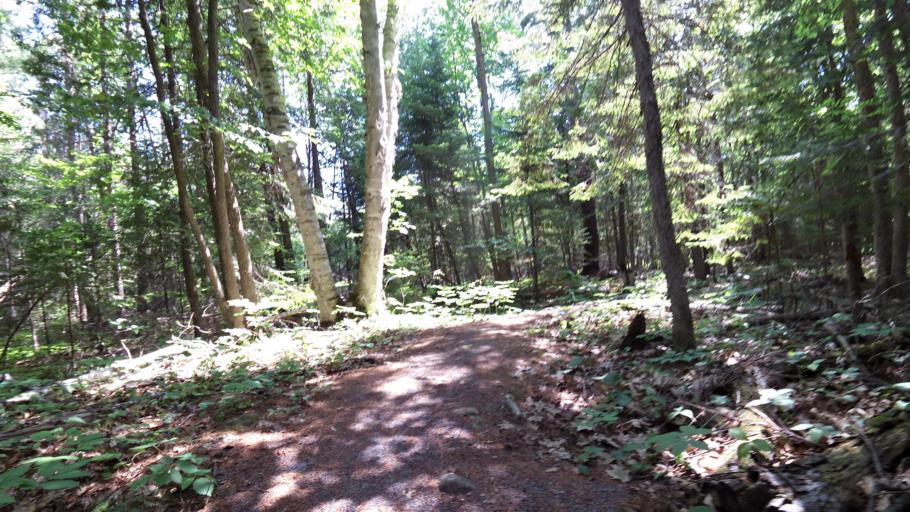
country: CA
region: Ontario
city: Arnprior
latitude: 45.4607
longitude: -76.2576
